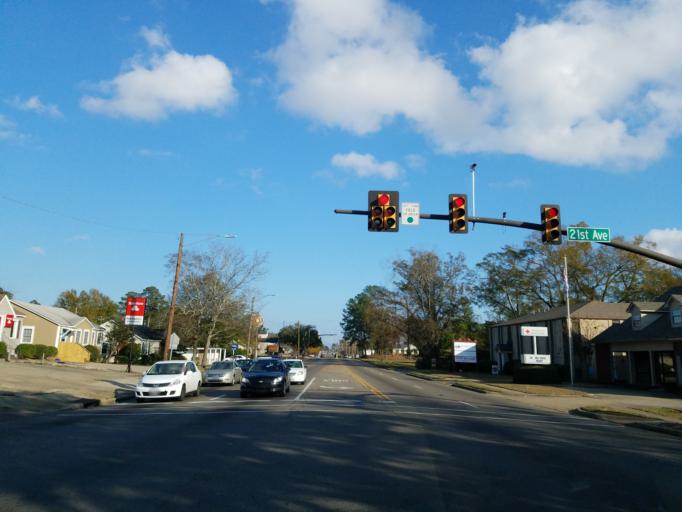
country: US
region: Mississippi
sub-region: Forrest County
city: Hattiesburg
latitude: 31.3247
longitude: -89.3228
